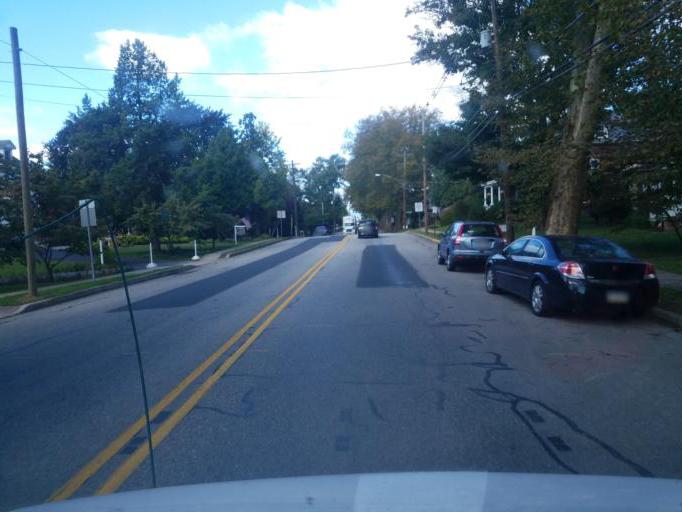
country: US
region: Pennsylvania
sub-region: Franklin County
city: Greencastle
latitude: 39.7878
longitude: -77.7176
